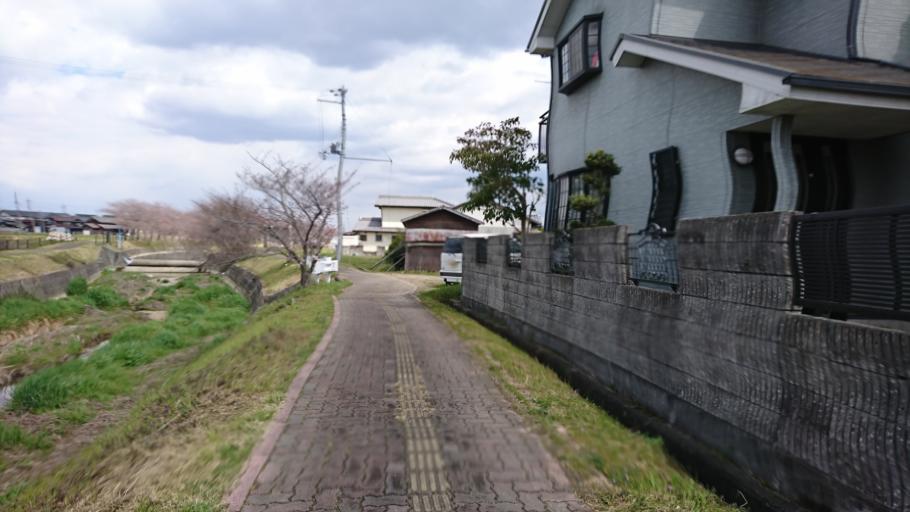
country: JP
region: Hyogo
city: Kakogawacho-honmachi
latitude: 34.7534
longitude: 134.8976
